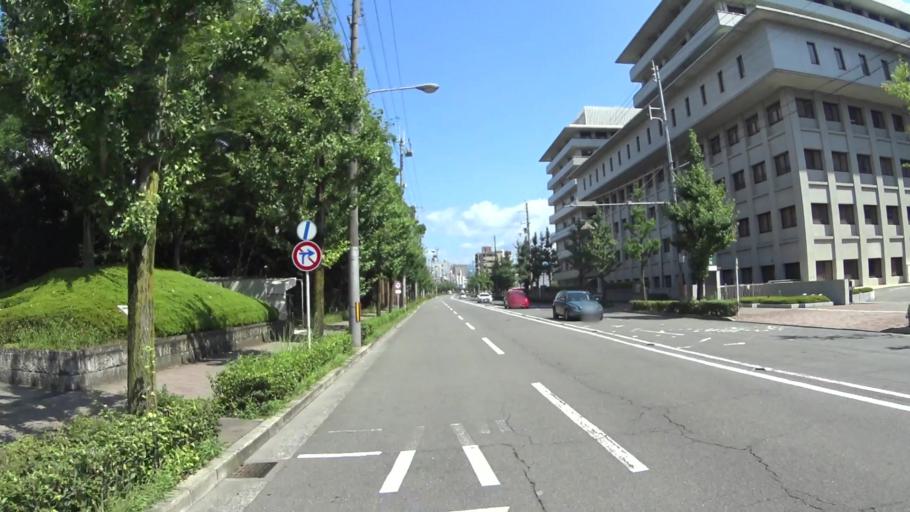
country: JP
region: Kyoto
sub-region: Kyoto-shi
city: Kamigyo-ku
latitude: 35.0235
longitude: 135.7692
